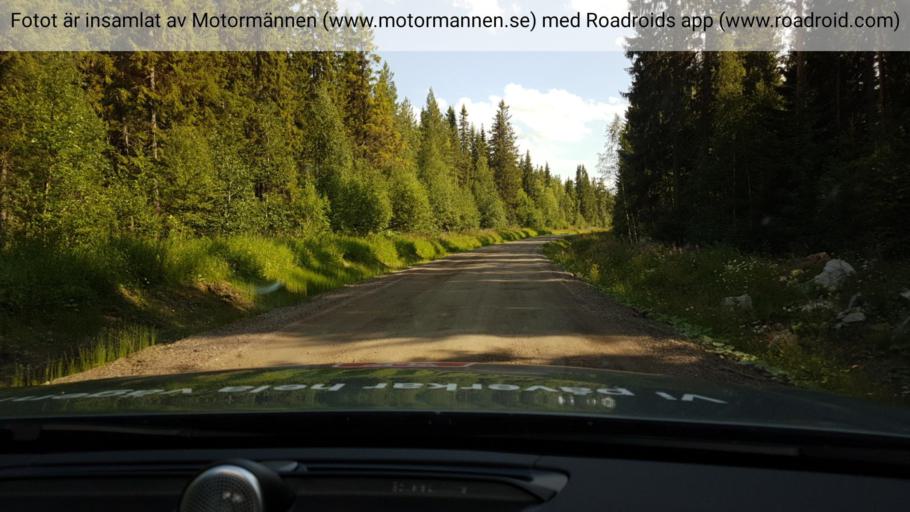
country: SE
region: Jaemtland
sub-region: Stroemsunds Kommun
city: Stroemsund
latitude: 64.0074
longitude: 15.9669
